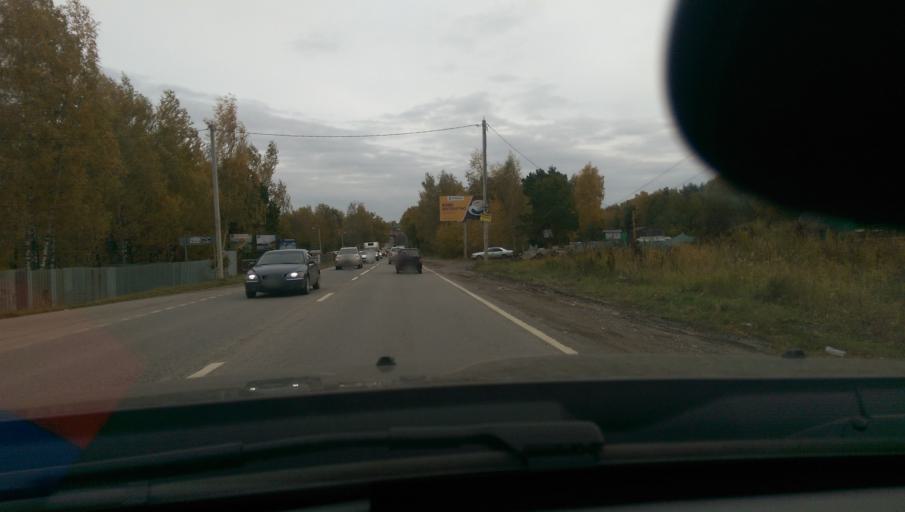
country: RU
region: Moskovskaya
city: Pirogovskiy
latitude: 55.9698
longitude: 37.7063
